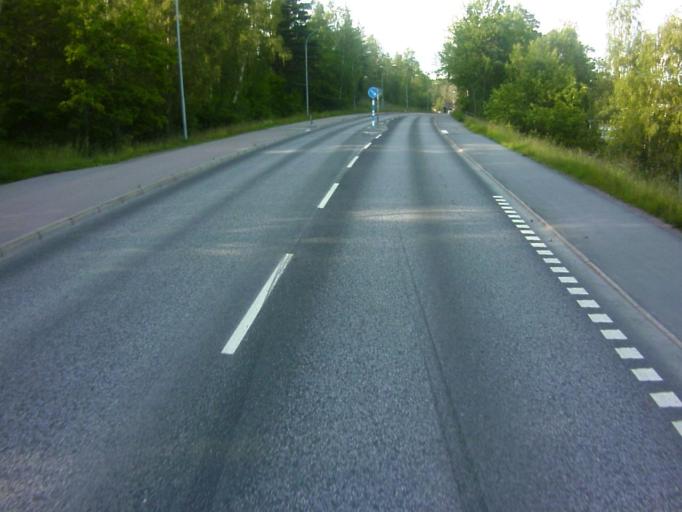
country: SE
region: Soedermanland
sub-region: Eskilstuna Kommun
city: Skogstorp
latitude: 59.3231
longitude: 16.4794
